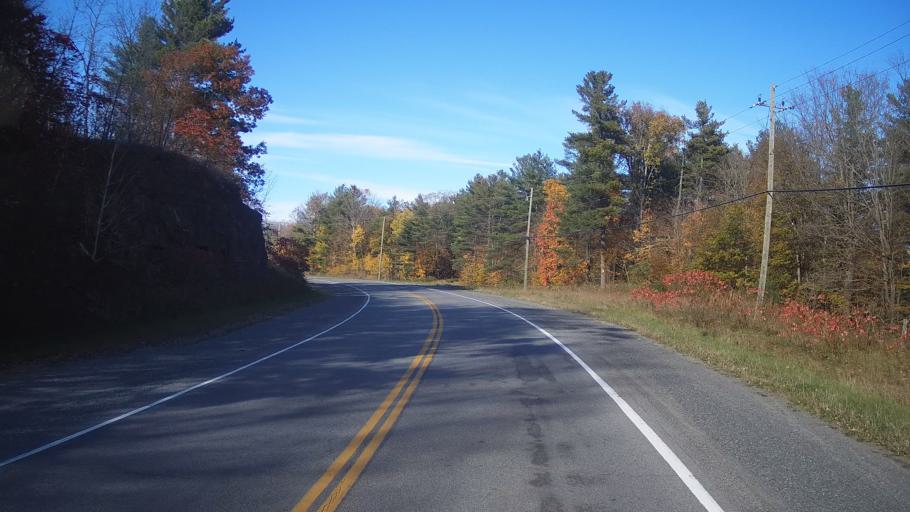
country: CA
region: Ontario
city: Kingston
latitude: 44.4916
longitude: -76.4780
